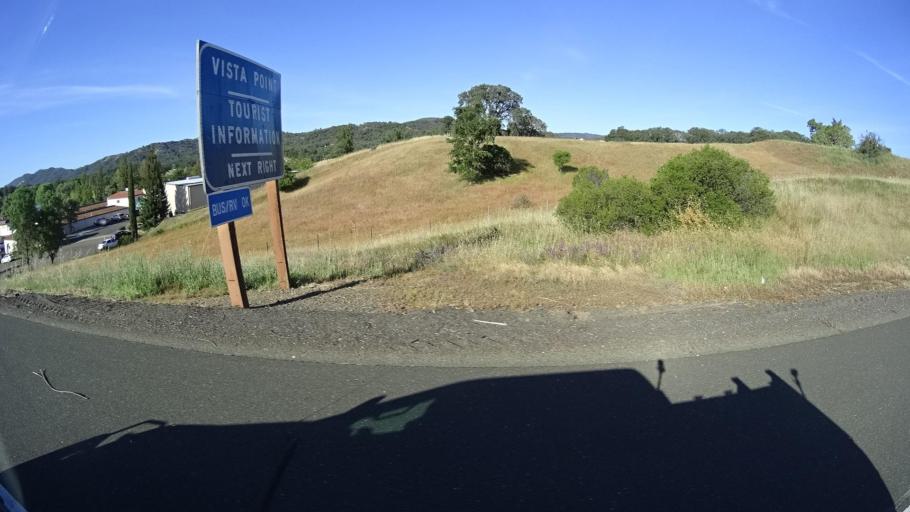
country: US
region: California
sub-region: Lake County
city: Lakeport
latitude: 39.0387
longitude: -122.9288
